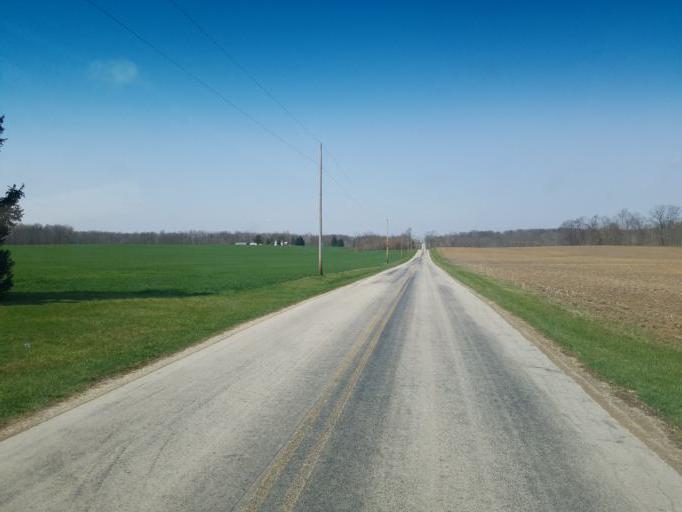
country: US
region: Ohio
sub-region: Wyandot County
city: Upper Sandusky
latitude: 40.8765
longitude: -83.2302
